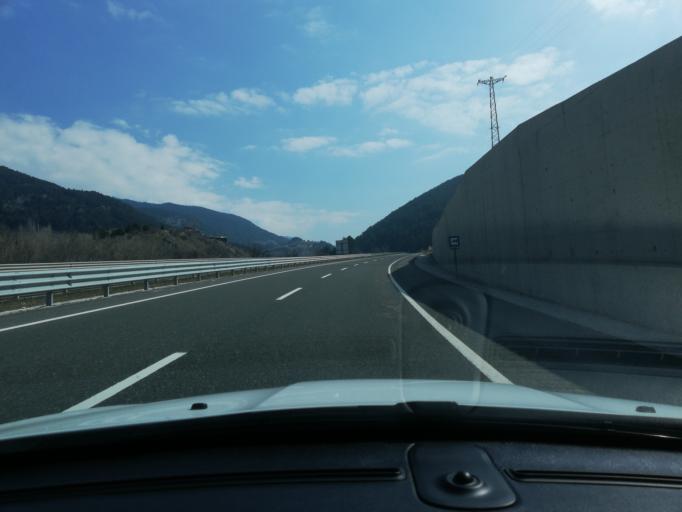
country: TR
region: Cankiri
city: Ilgaz
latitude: 41.0279
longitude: 33.7277
